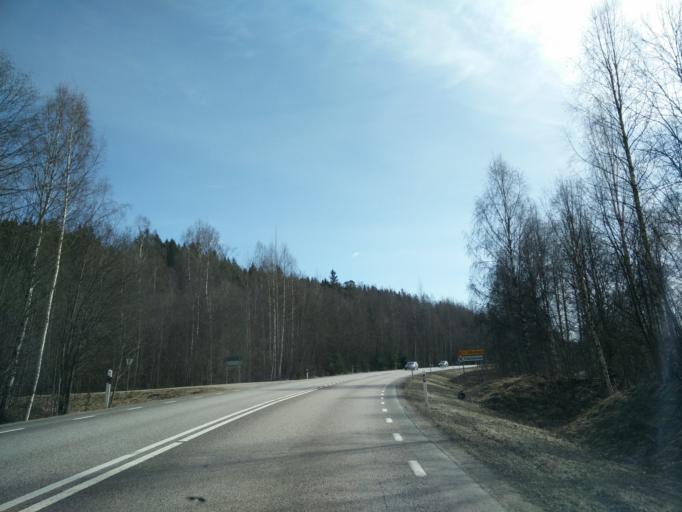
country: SE
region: Vaermland
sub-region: Hagfors Kommun
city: Hagfors
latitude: 60.0361
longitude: 13.5998
